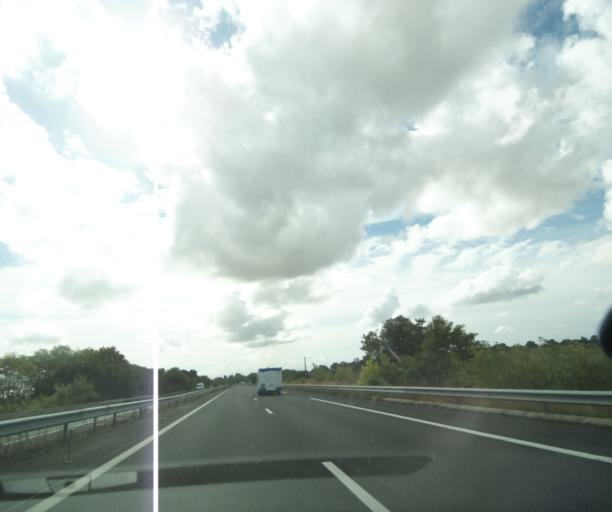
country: FR
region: Poitou-Charentes
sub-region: Departement de la Charente-Maritime
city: Chermignac
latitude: 45.7129
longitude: -0.6565
